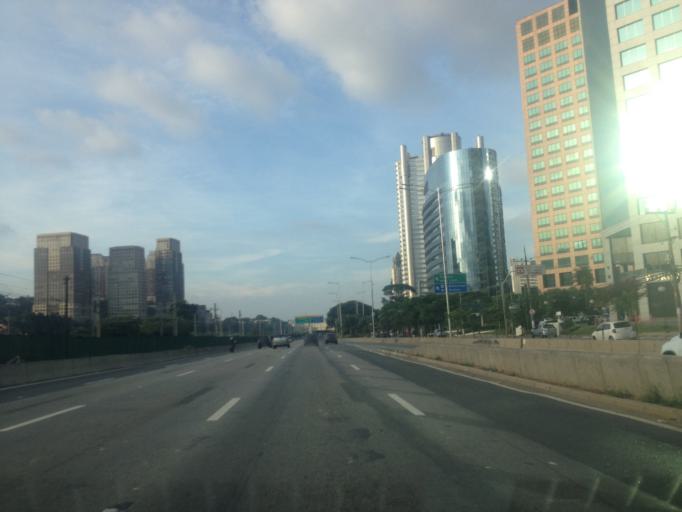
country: BR
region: Sao Paulo
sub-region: Sao Paulo
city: Sao Paulo
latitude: -23.6095
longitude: -46.6979
